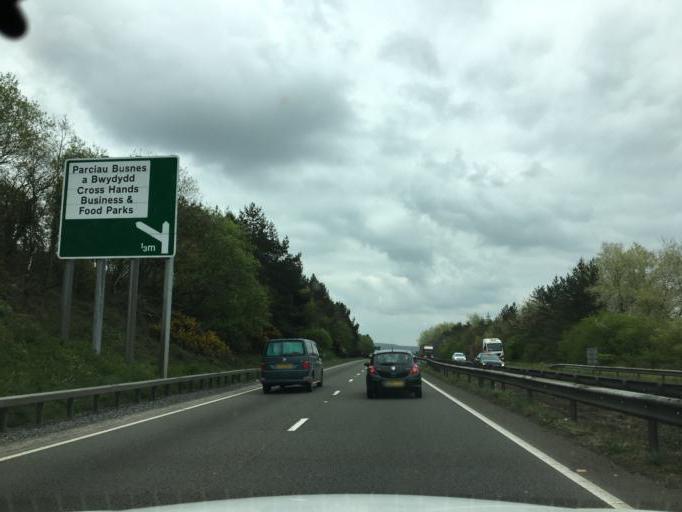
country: GB
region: Wales
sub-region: Carmarthenshire
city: Cross Hands
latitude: 51.7955
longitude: -4.0817
